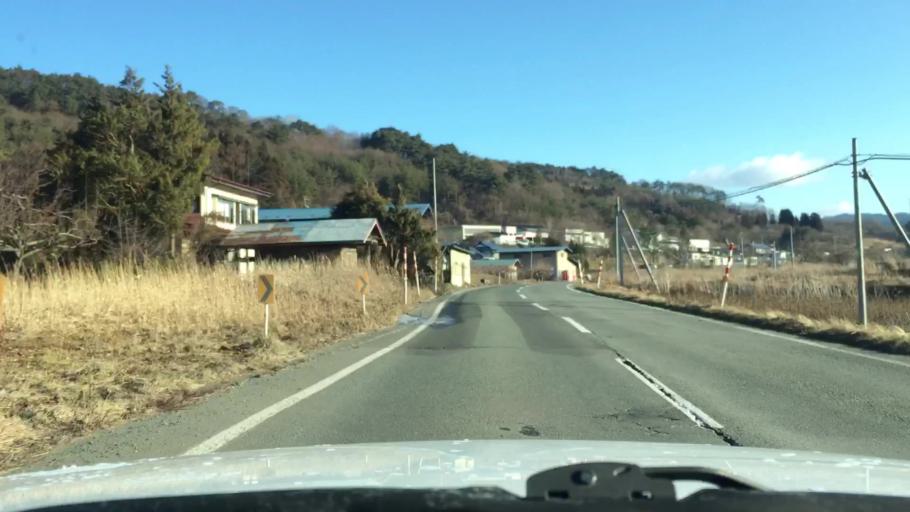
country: JP
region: Iwate
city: Morioka-shi
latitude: 39.6600
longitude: 141.1938
